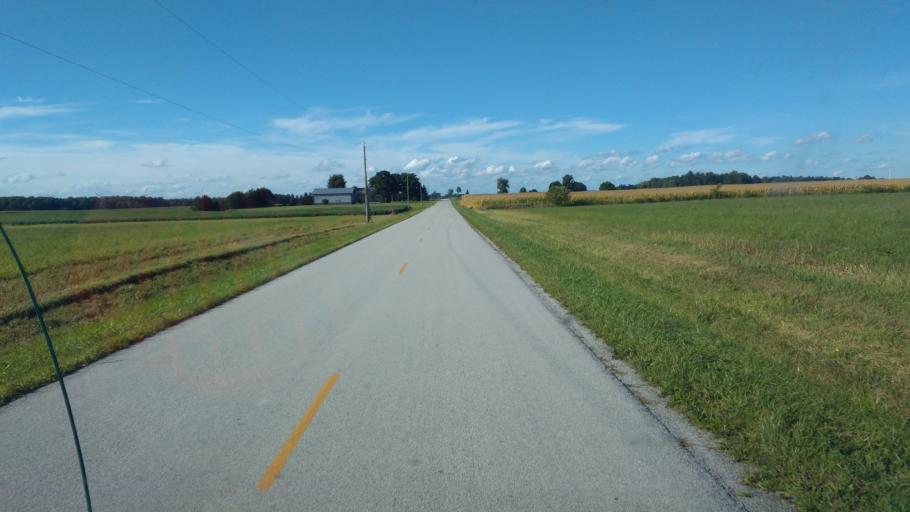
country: US
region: Ohio
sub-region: Hardin County
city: Kenton
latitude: 40.7494
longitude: -83.6906
